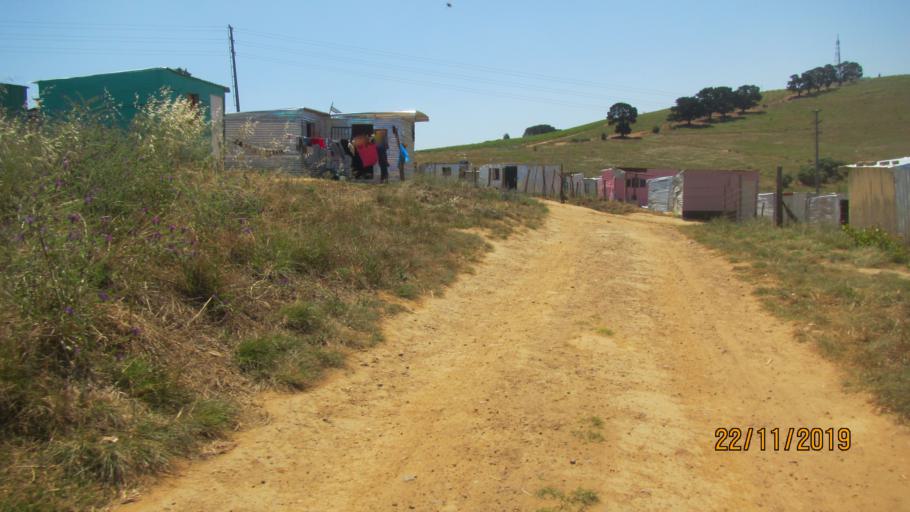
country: ZA
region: Western Cape
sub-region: Cape Winelands District Municipality
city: Stellenbosch
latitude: -33.9210
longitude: 18.8360
